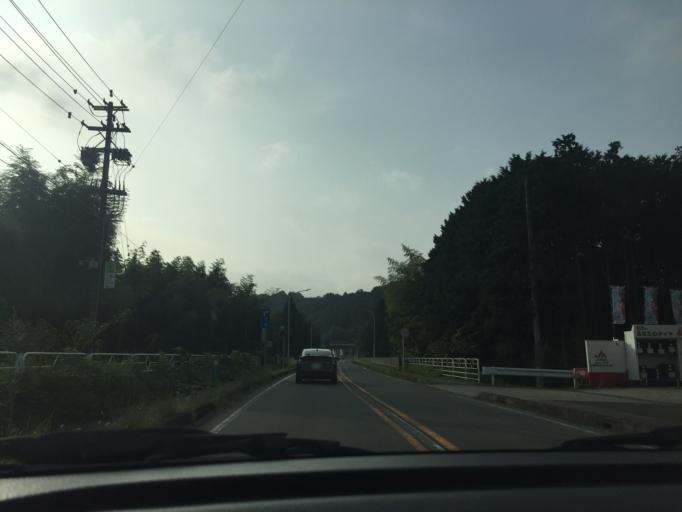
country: JP
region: Aichi
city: Shinshiro
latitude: 34.9247
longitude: 137.5541
